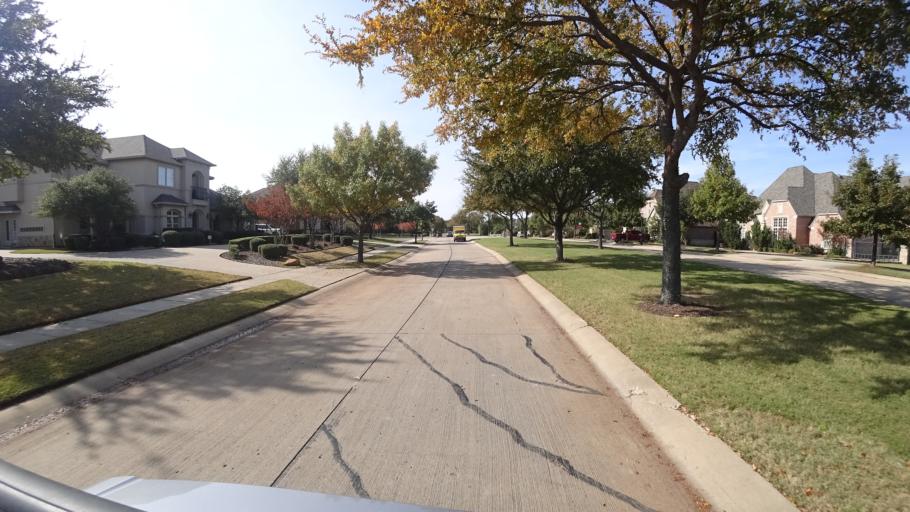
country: US
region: Texas
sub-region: Denton County
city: The Colony
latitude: 33.0369
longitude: -96.8896
